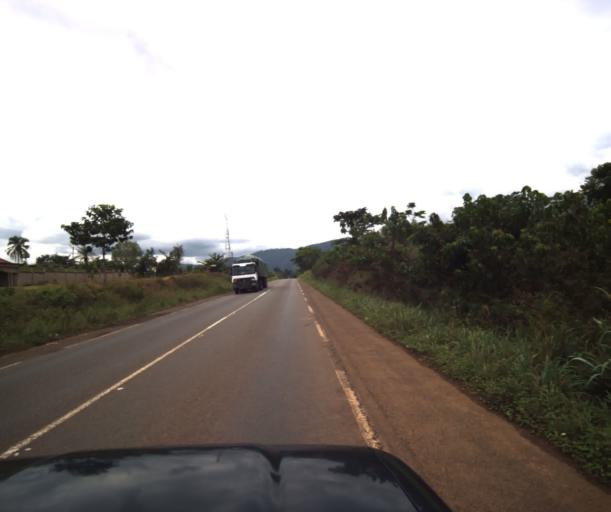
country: CM
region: Centre
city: Eseka
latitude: 3.8782
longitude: 10.8138
